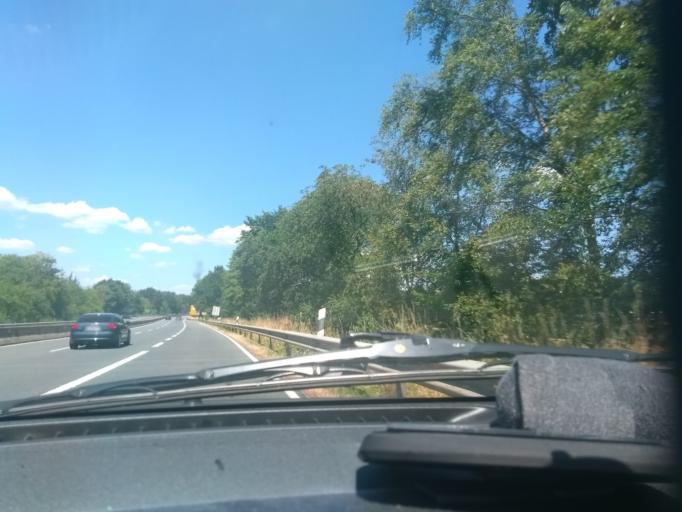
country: DE
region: Lower Saxony
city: Meppen
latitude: 52.7041
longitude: 7.2900
